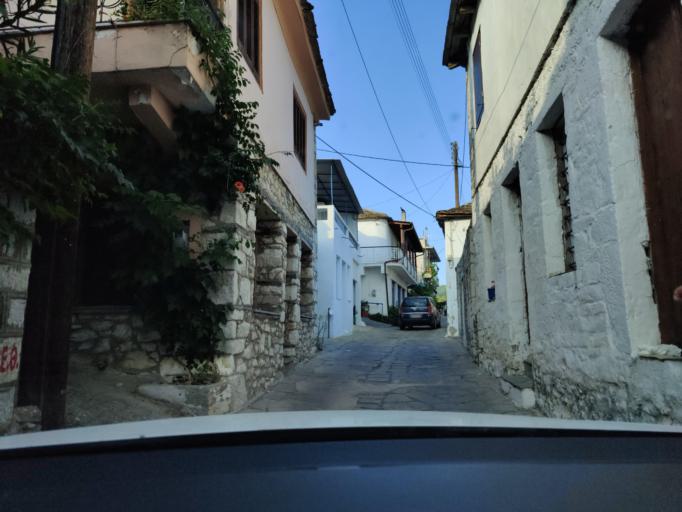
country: GR
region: East Macedonia and Thrace
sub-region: Nomos Kavalas
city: Potamia
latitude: 40.6602
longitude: 24.6943
